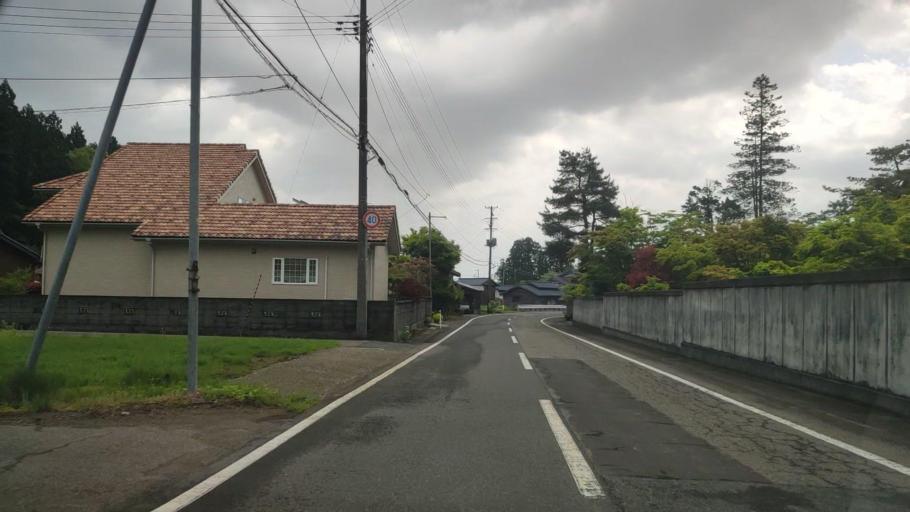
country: JP
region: Niigata
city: Gosen
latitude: 37.7241
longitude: 139.1313
